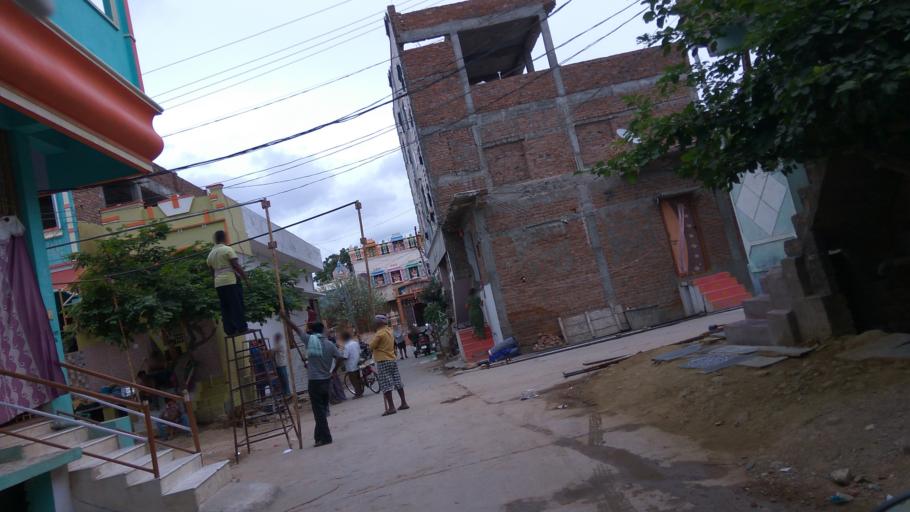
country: IN
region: Andhra Pradesh
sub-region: Prakasam
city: Cumbum
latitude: 15.5516
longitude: 79.1008
